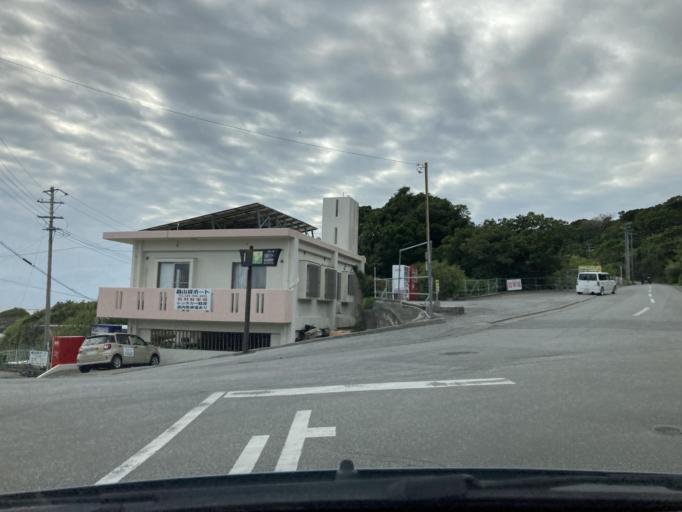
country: JP
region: Okinawa
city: Tomigusuku
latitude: 26.1349
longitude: 127.7913
